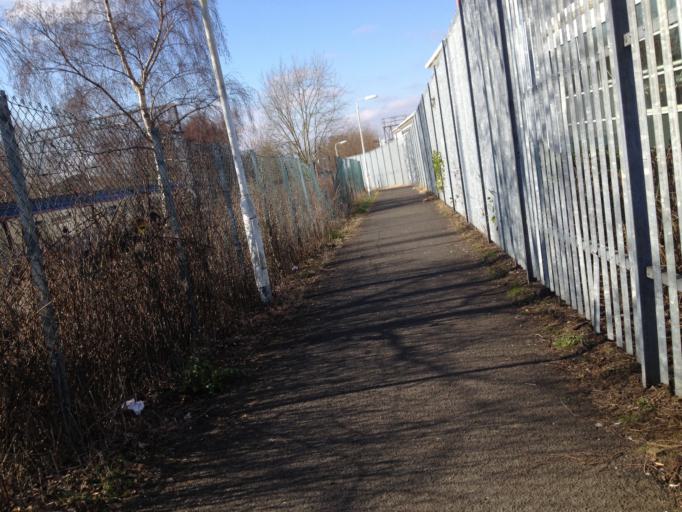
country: GB
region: Scotland
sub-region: South Lanarkshire
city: Bothwell
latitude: 55.7802
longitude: -4.0565
